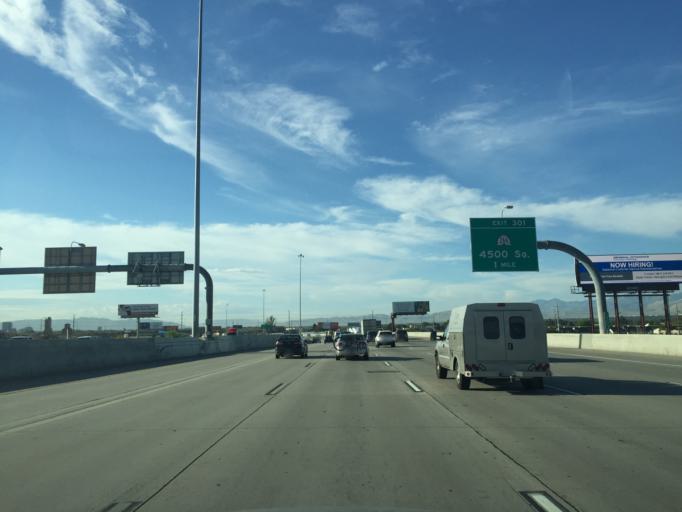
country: US
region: Utah
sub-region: Salt Lake County
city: Centerfield
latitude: 40.6940
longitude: -111.9027
